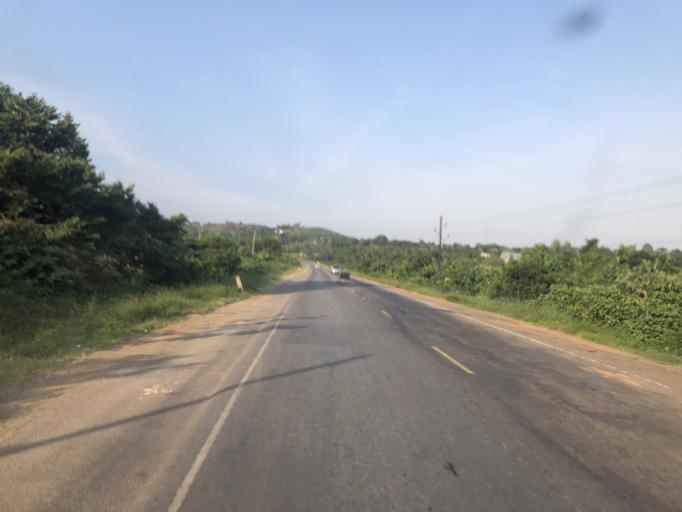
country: UG
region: Central Region
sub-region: Mpigi District
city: Mpigi
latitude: 0.1648
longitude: 32.2523
